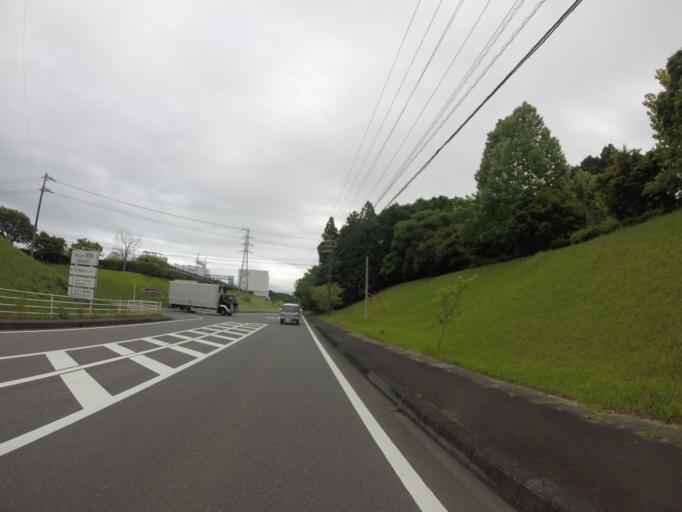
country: JP
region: Shizuoka
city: Sagara
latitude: 34.7324
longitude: 138.1846
